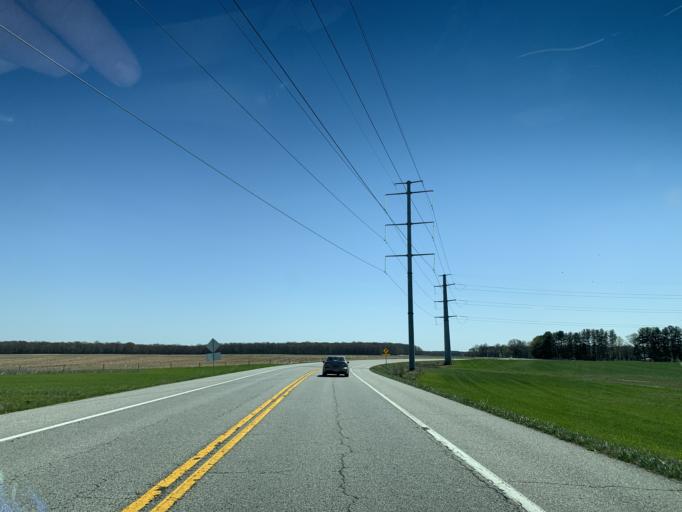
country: US
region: Maryland
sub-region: Queen Anne's County
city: Centreville
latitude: 38.9954
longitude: -76.0446
